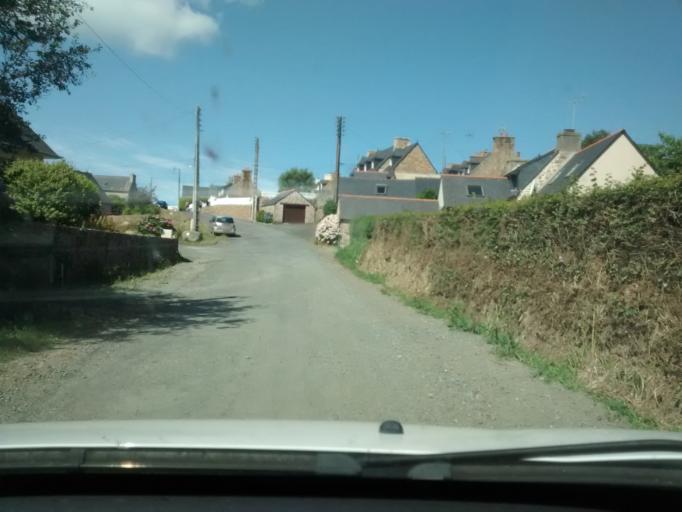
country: FR
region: Brittany
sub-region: Departement des Cotes-d'Armor
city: Trevou-Treguignec
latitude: 48.8336
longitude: -3.3193
